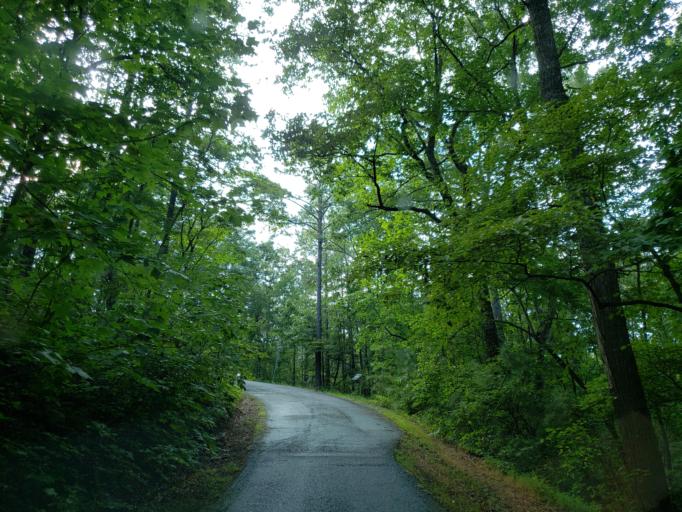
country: US
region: Georgia
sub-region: Bartow County
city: Emerson
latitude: 34.1954
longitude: -84.6499
